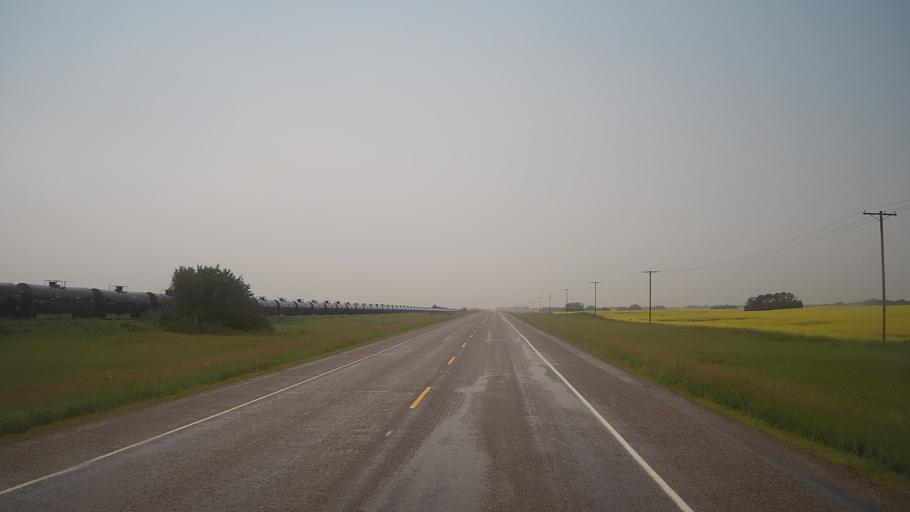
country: CA
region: Saskatchewan
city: Biggar
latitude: 52.1599
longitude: -108.2751
